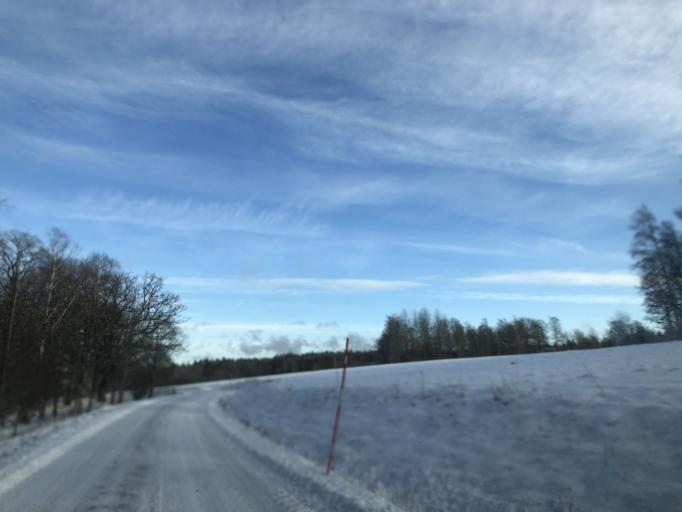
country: SE
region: Vaestra Goetaland
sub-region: Ulricehamns Kommun
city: Ulricehamn
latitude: 57.7269
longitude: 13.4635
